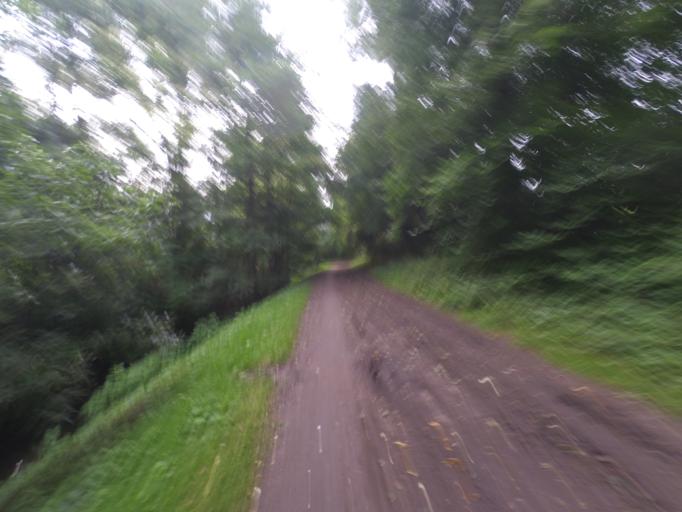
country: DE
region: Hamburg
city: Wandsbek
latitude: 53.5483
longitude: 10.1198
